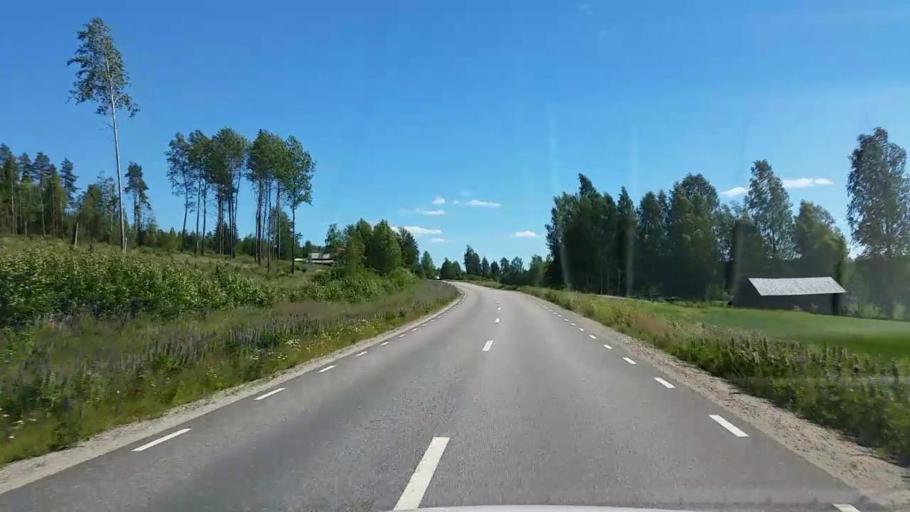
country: SE
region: Gaevleborg
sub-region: Ovanakers Kommun
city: Edsbyn
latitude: 61.4154
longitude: 15.7554
